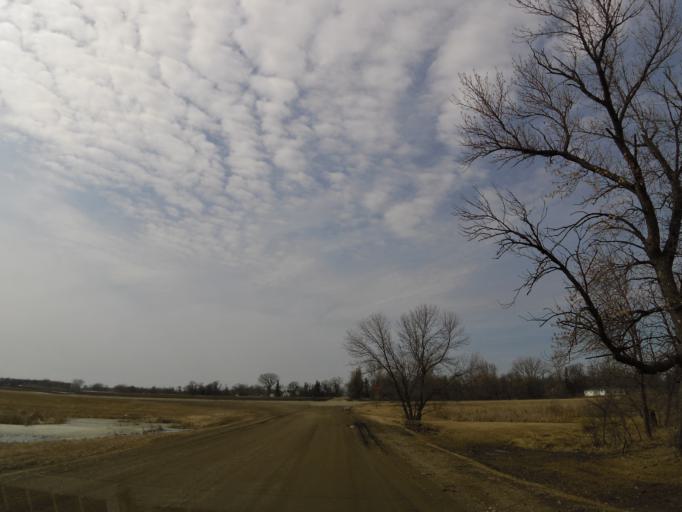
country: US
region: North Dakota
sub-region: Walsh County
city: Grafton
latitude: 48.2814
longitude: -97.3671
